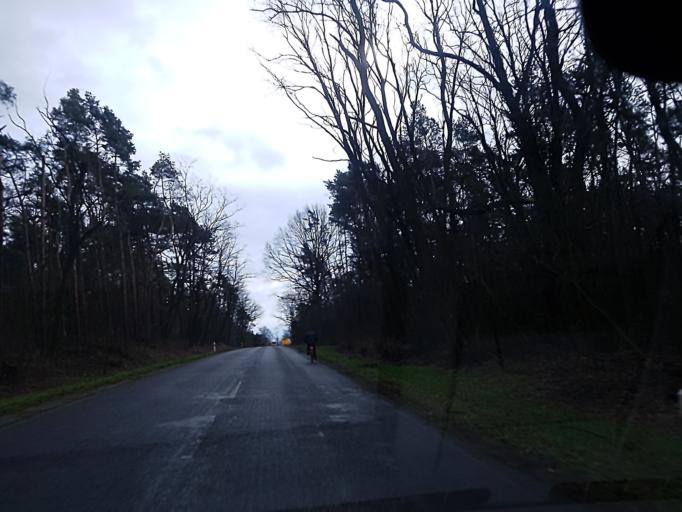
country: DE
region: Brandenburg
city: Elsterwerda
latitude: 51.4810
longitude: 13.5026
